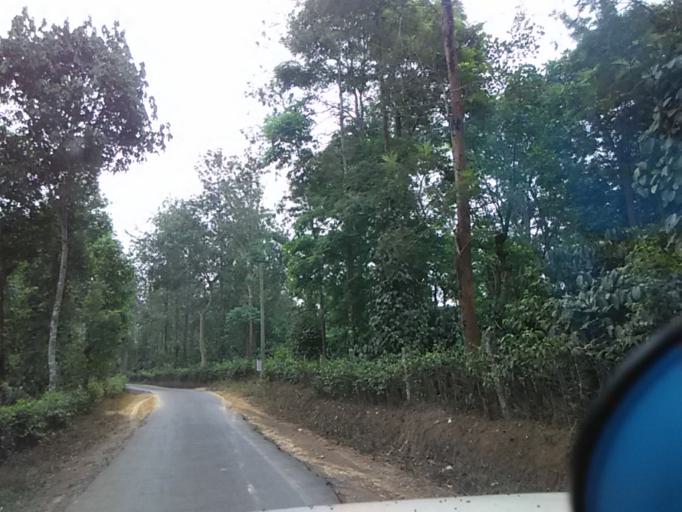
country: IN
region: Karnataka
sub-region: Kodagu
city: Virarajendrapet
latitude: 12.2133
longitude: 75.7381
